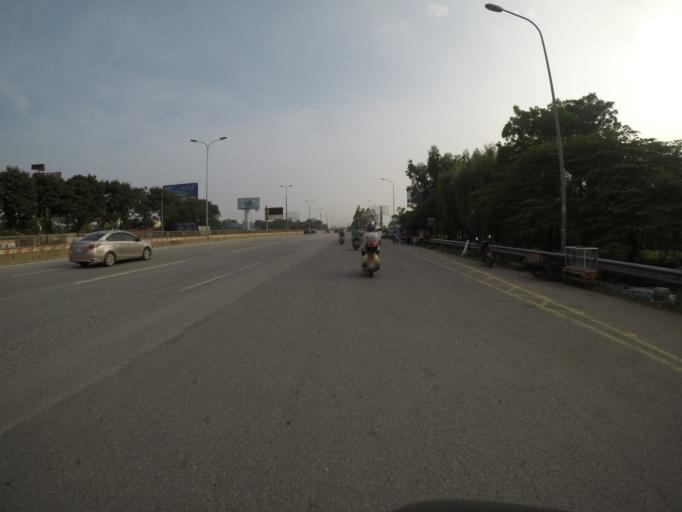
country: VN
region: Ha Noi
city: Me Linh
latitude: 21.1865
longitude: 105.7803
